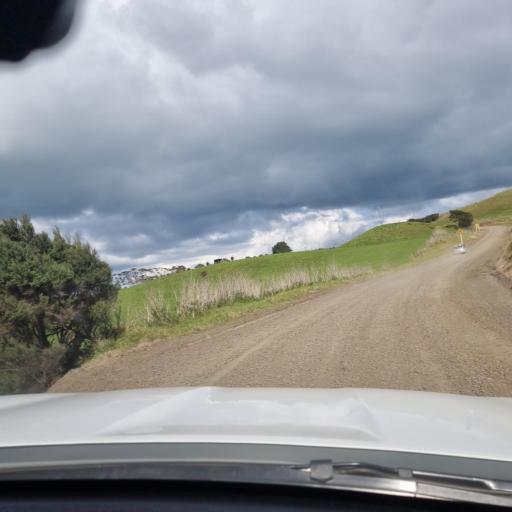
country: NZ
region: Auckland
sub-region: Auckland
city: Wellsford
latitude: -36.3494
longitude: 174.1717
